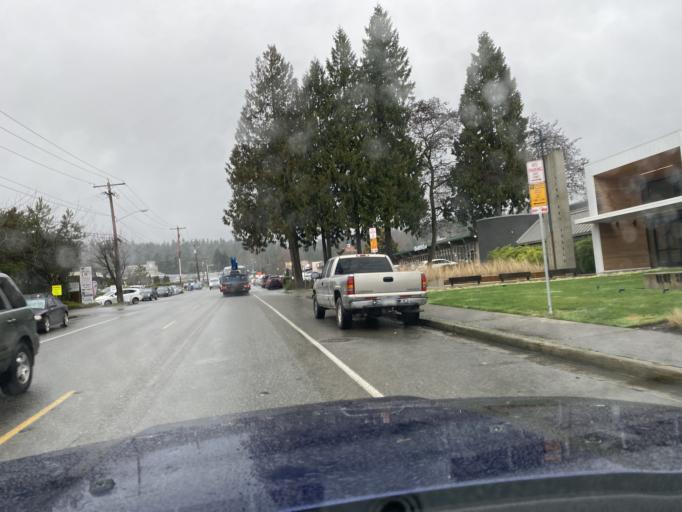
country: US
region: Washington
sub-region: King County
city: Bellevue
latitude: 47.6258
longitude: -122.1670
